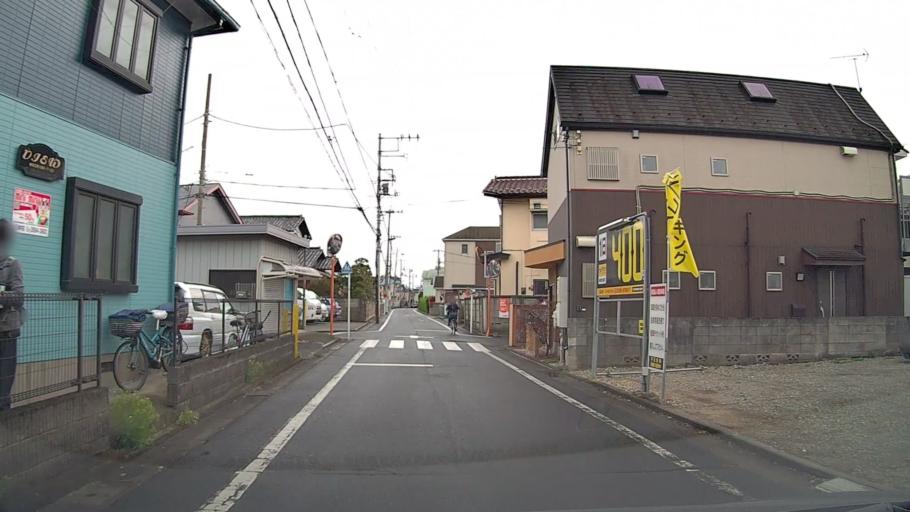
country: JP
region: Tokyo
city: Musashino
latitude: 35.7414
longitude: 139.5811
